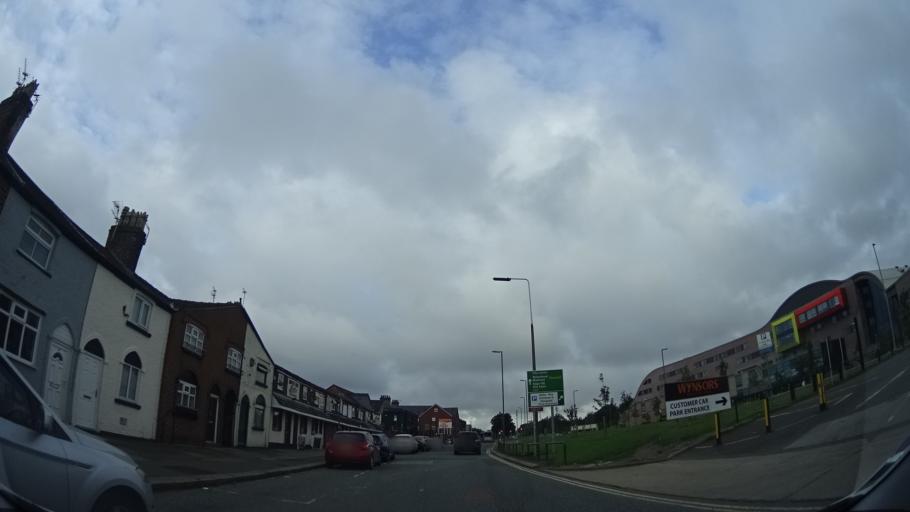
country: GB
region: England
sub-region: Knowsley
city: Knowsley
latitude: 53.4176
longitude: -2.8945
